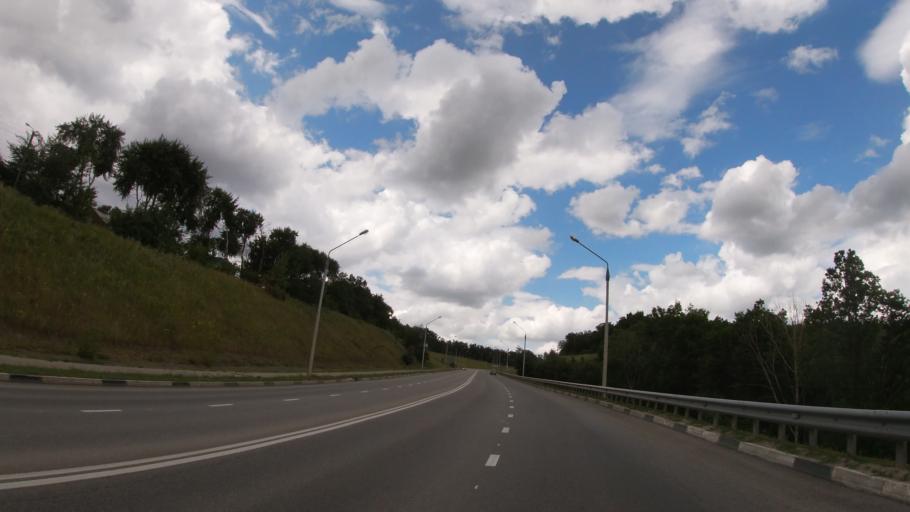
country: RU
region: Belgorod
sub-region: Belgorodskiy Rayon
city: Belgorod
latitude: 50.6209
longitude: 36.6156
